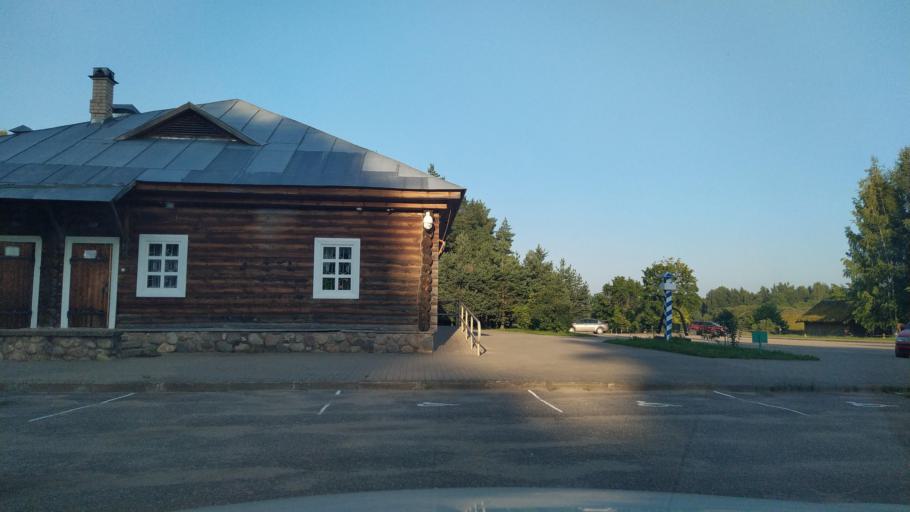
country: RU
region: Pskov
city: Pushkinskiye Gory
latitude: 57.0476
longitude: 28.9147
